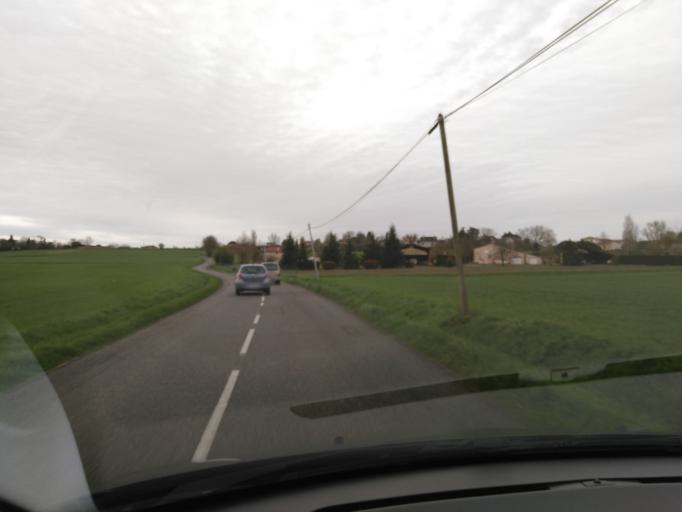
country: FR
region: Midi-Pyrenees
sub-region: Departement de la Haute-Garonne
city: Lapeyrouse-Fossat
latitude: 43.7088
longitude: 1.5124
